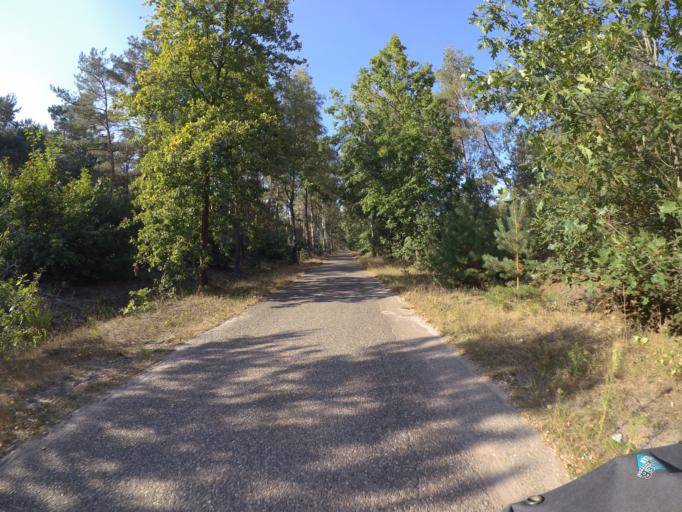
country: NL
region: North Brabant
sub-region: Gemeente Oirschot
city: Oirschot
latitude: 51.4749
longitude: 5.3289
